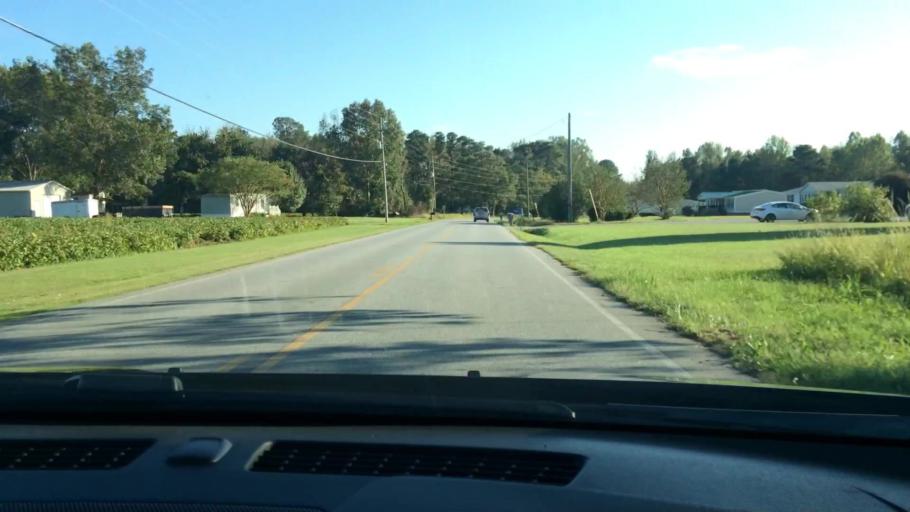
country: US
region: North Carolina
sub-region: Pitt County
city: Winterville
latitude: 35.5267
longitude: -77.4423
